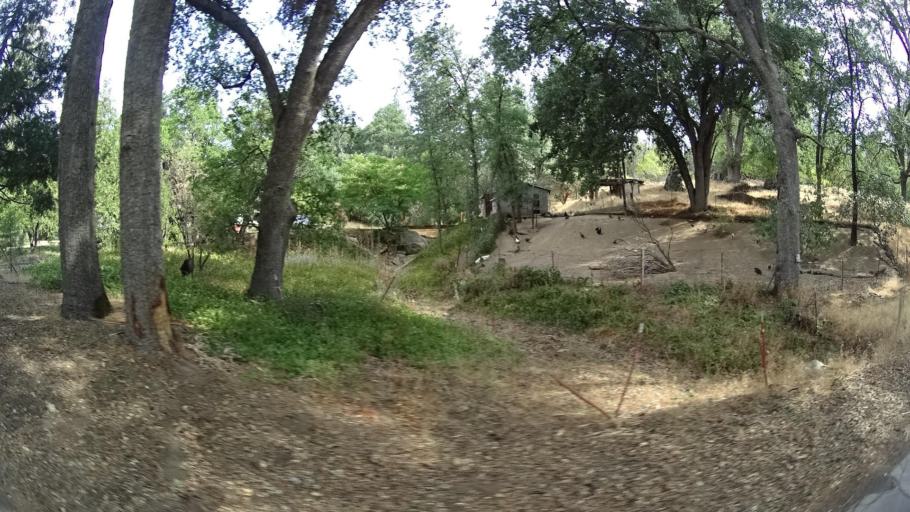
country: US
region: California
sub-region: Mariposa County
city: Midpines
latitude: 37.5106
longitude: -119.8264
